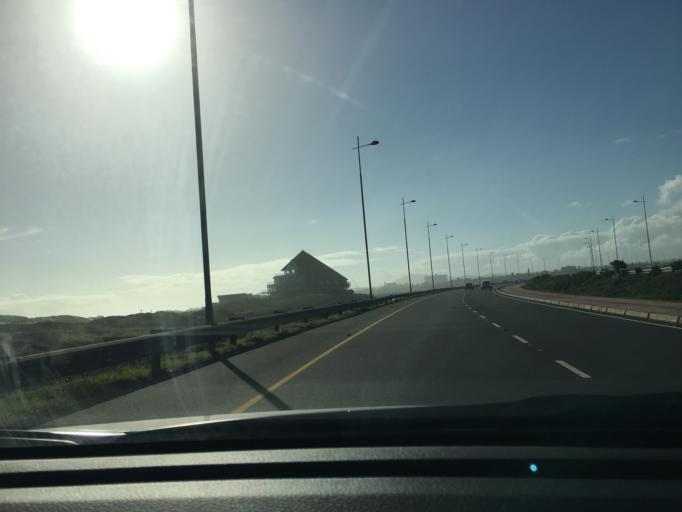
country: ZA
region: Western Cape
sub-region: City of Cape Town
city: Sunset Beach
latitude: -33.8351
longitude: 18.4842
